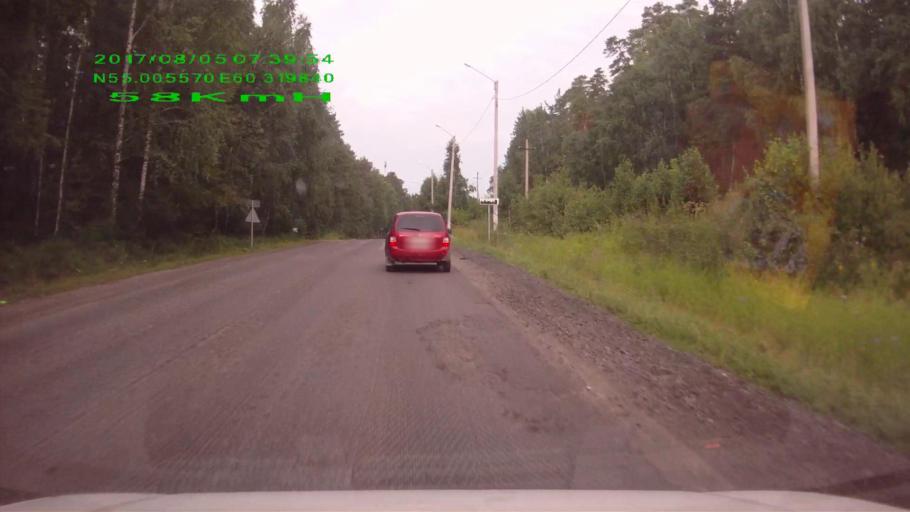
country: RU
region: Chelyabinsk
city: Chebarkul'
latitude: 55.0056
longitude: 60.3195
